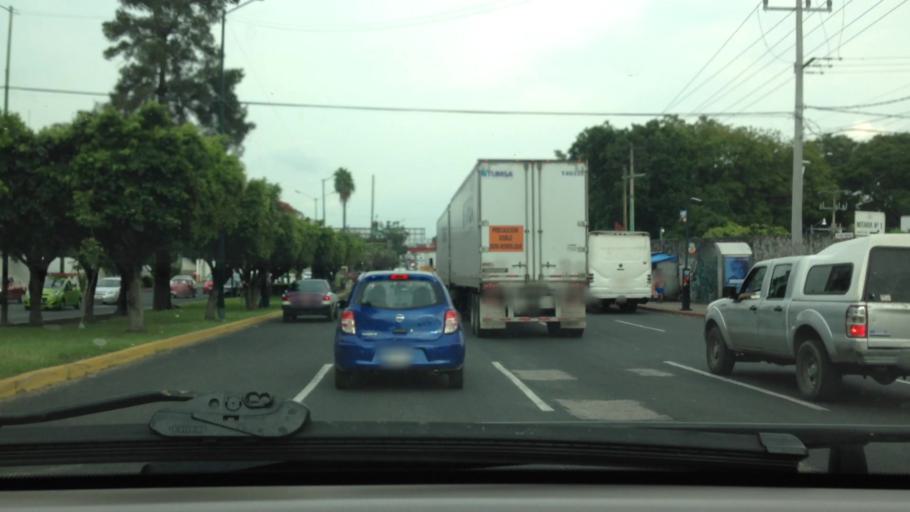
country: MX
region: Morelos
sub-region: Tepoztlan
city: Loma Bonita
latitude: 18.9199
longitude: -99.1936
